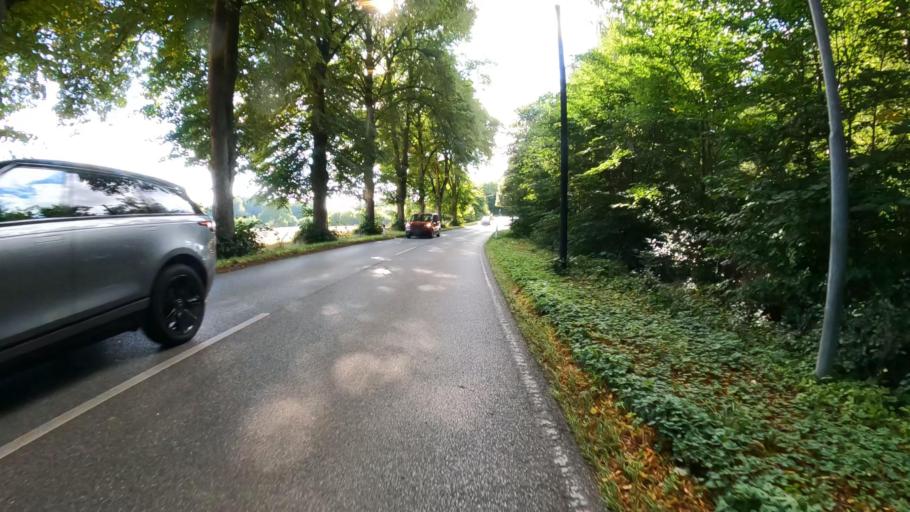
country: DE
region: Schleswig-Holstein
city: Hoisdorf
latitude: 53.6577
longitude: 10.3010
